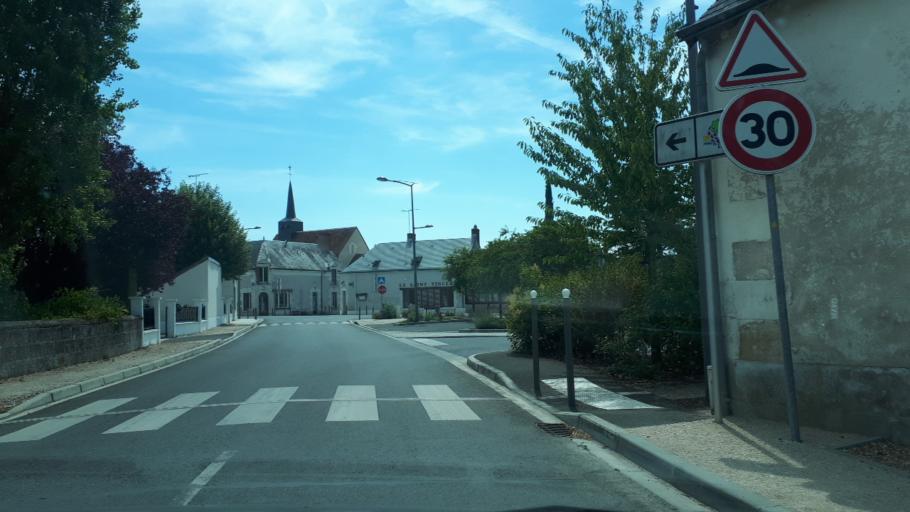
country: FR
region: Centre
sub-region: Departement du Loir-et-Cher
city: Contres
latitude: 47.3905
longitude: 1.3769
